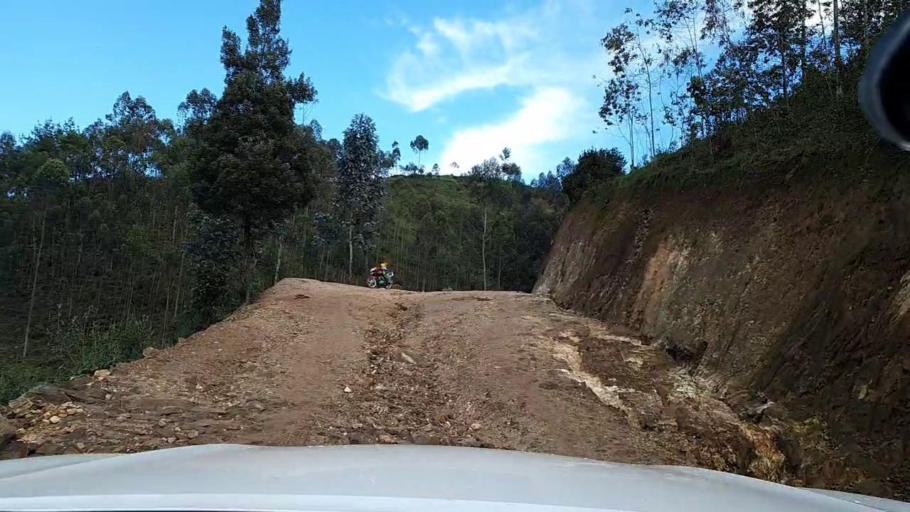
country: BI
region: Kayanza
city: Kayanza
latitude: -2.7814
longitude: 29.4539
